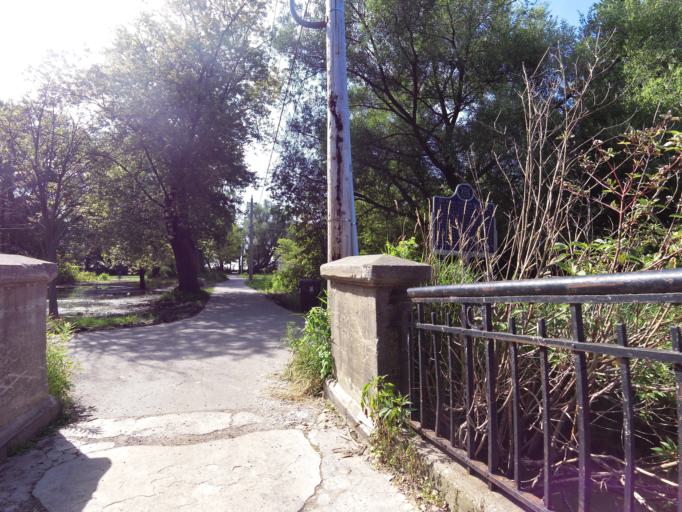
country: CA
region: Ontario
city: Toronto
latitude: 43.6215
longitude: -79.3658
